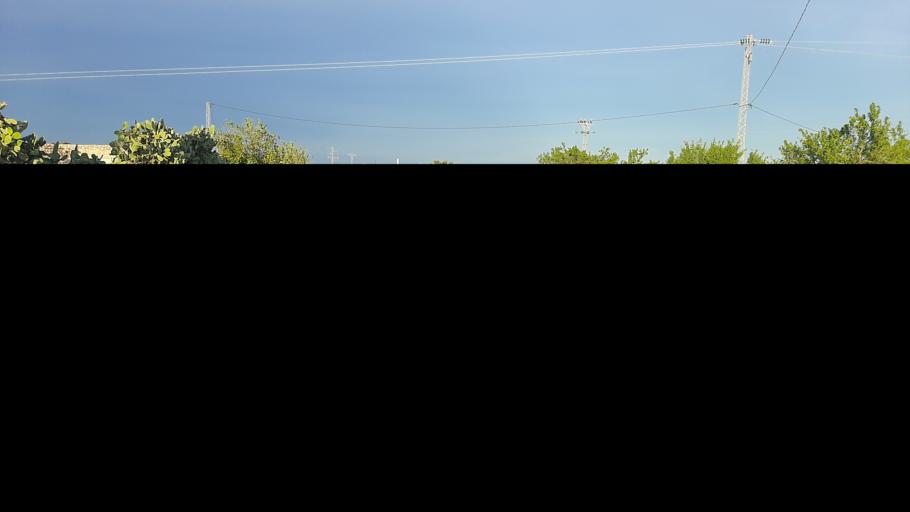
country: TN
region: Safaqis
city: Sfax
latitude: 34.9465
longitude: 10.5186
